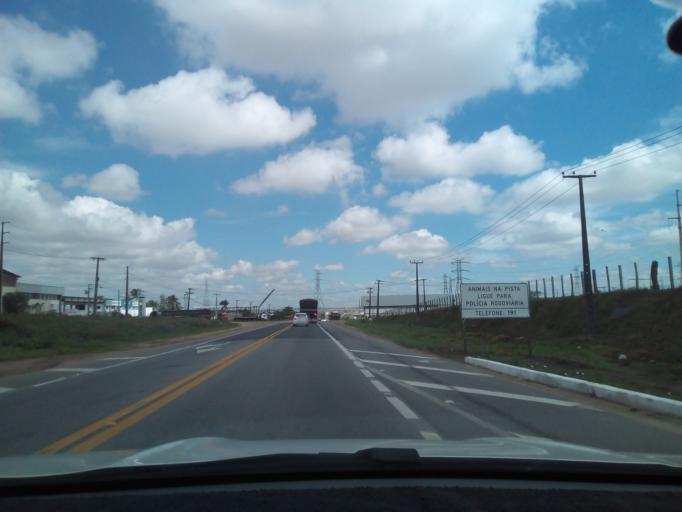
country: BR
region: Paraiba
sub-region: Campina Grande
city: Campina Grande
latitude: -7.2747
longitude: -35.9059
